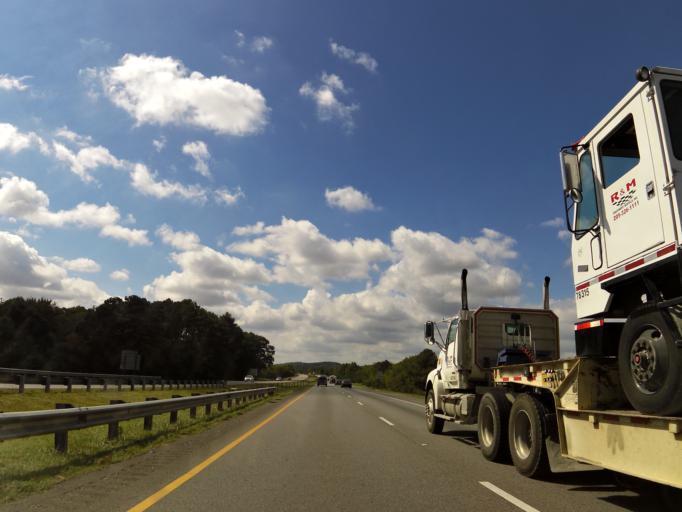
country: US
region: Alabama
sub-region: Jefferson County
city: Bessemer
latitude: 33.4030
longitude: -86.9773
